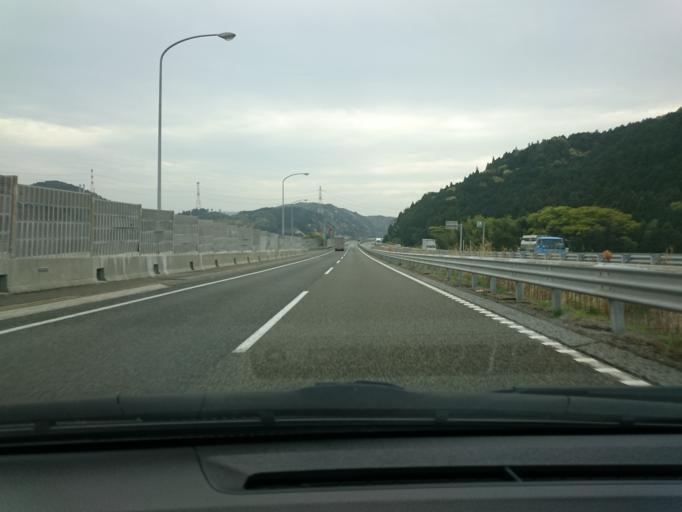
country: JP
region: Gifu
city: Tarui
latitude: 35.3465
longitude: 136.4260
